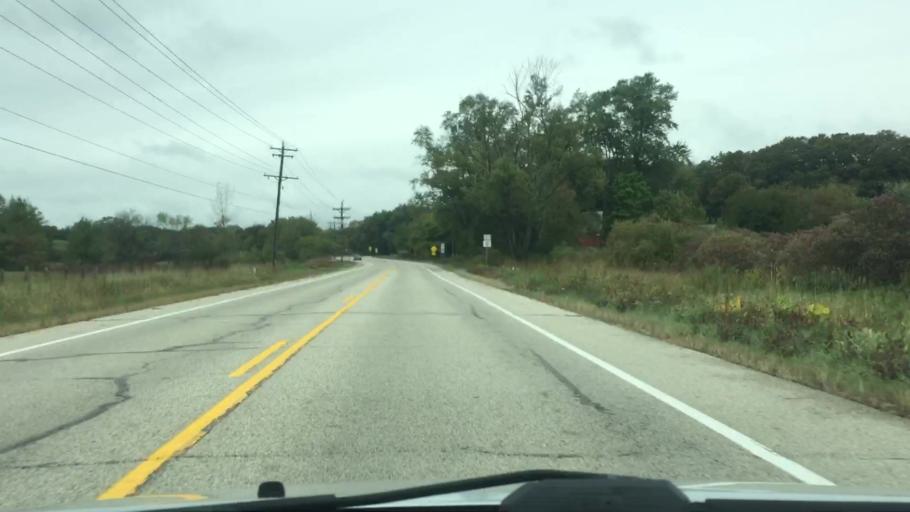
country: US
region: Wisconsin
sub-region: Waukesha County
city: Eagle
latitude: 42.8574
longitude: -88.4987
